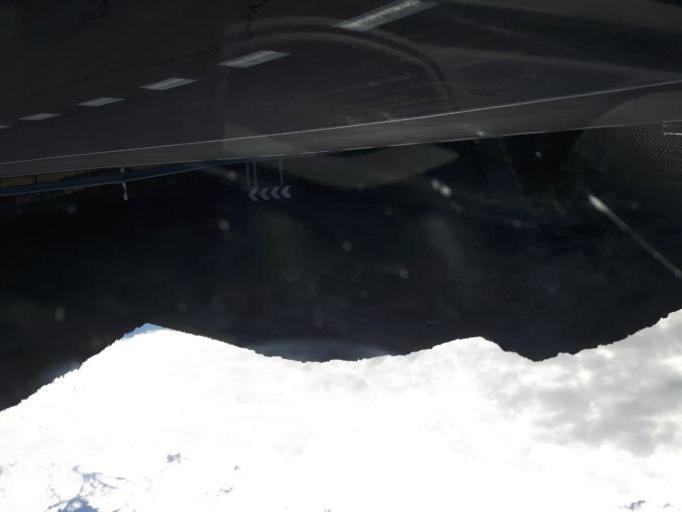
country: ES
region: Castille and Leon
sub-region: Provincia de Avila
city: Mengamunoz
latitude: 40.4877
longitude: -5.0054
